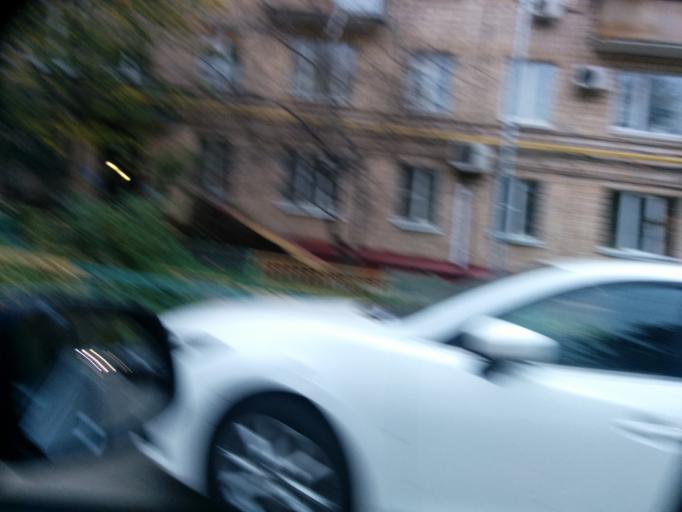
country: RU
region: Moskovskaya
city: Dorogomilovo
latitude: 55.7729
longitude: 37.5834
